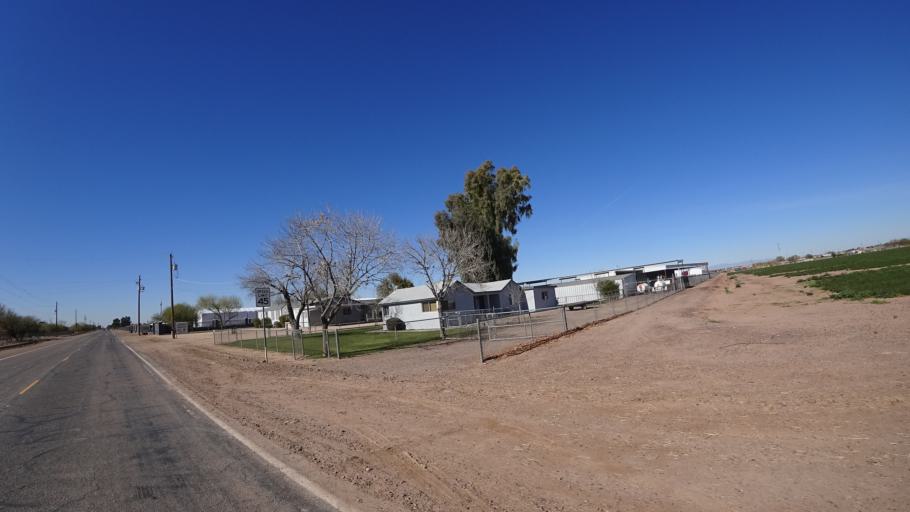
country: US
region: Arizona
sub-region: Maricopa County
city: Avondale
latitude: 33.3918
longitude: -112.3145
